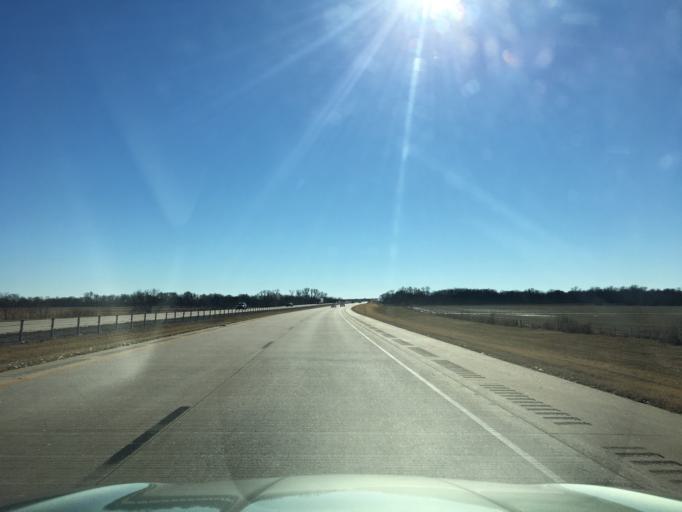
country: US
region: Oklahoma
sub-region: Kay County
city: Tonkawa
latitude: 36.4836
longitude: -97.3275
